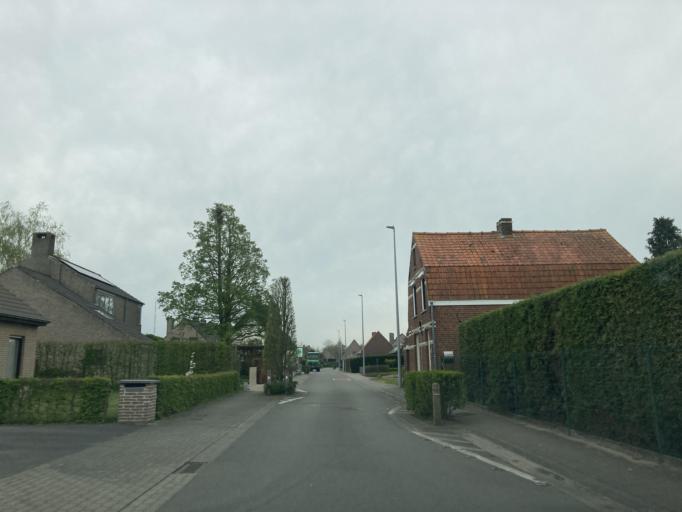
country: BE
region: Flanders
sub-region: Provincie West-Vlaanderen
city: Wingene
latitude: 51.0417
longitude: 3.2228
